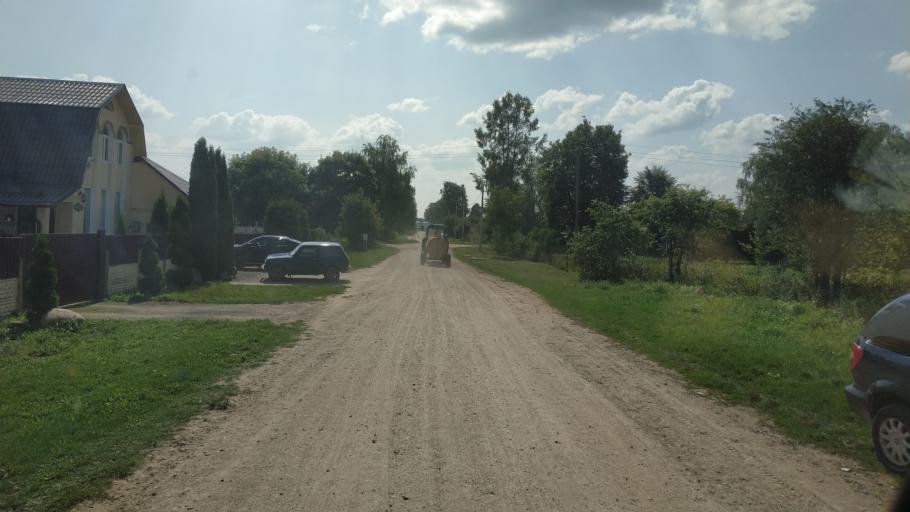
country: BY
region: Mogilev
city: Buynichy
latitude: 53.9656
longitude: 30.1936
